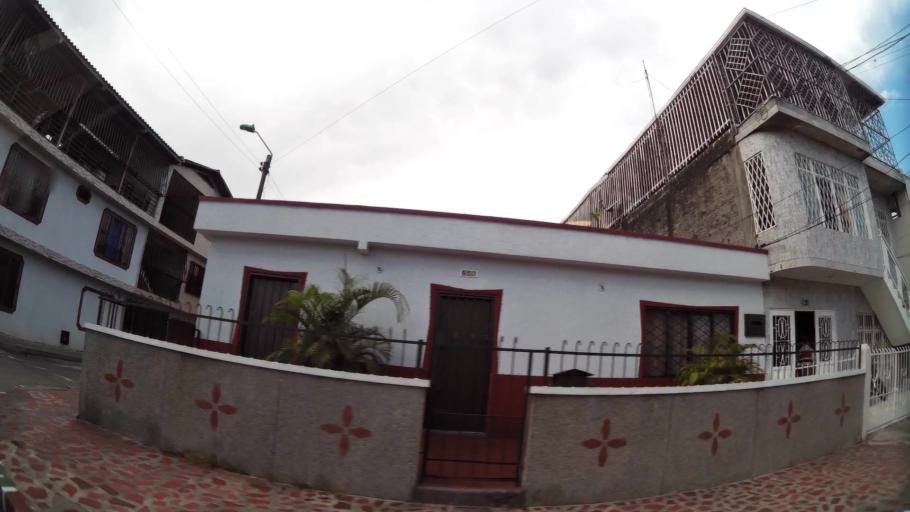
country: CO
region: Valle del Cauca
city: Cali
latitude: 3.4235
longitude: -76.5233
